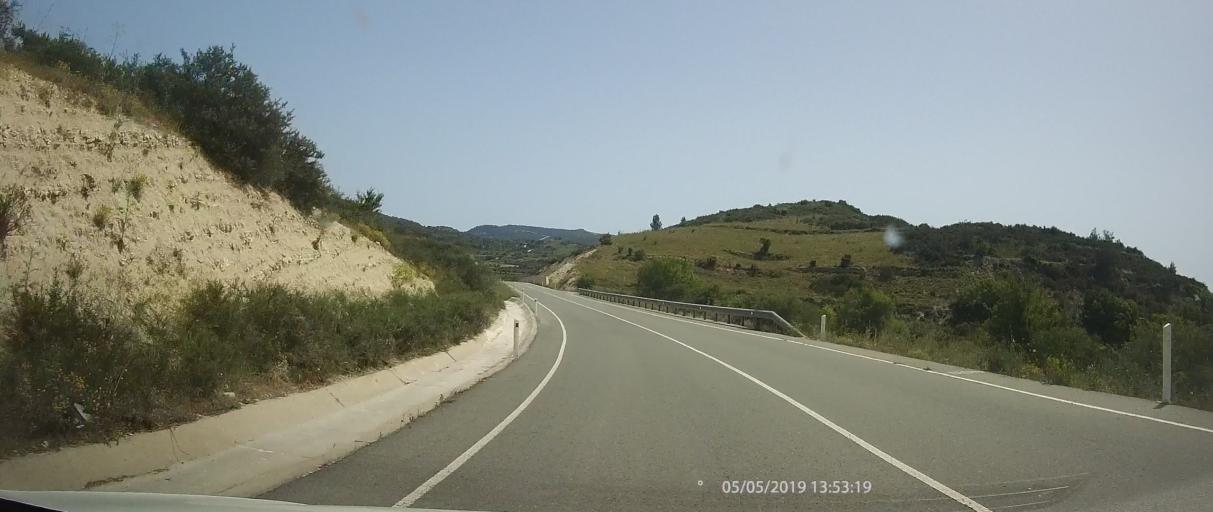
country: CY
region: Limassol
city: Pachna
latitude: 34.8222
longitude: 32.7244
